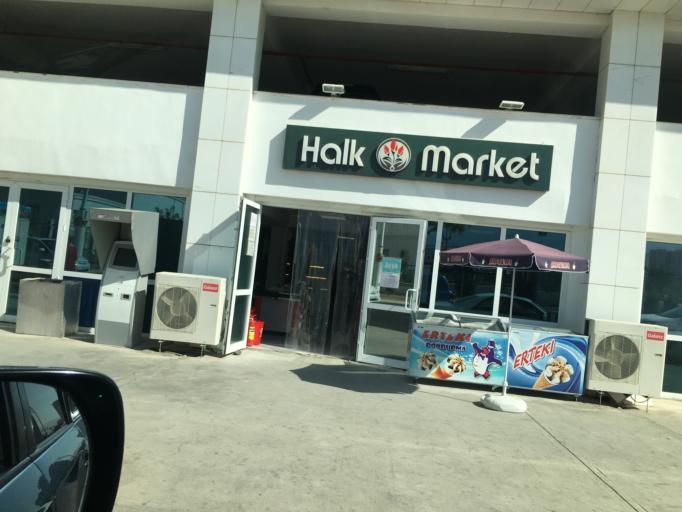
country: TM
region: Ahal
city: Ashgabat
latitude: 37.9287
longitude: 58.3673
